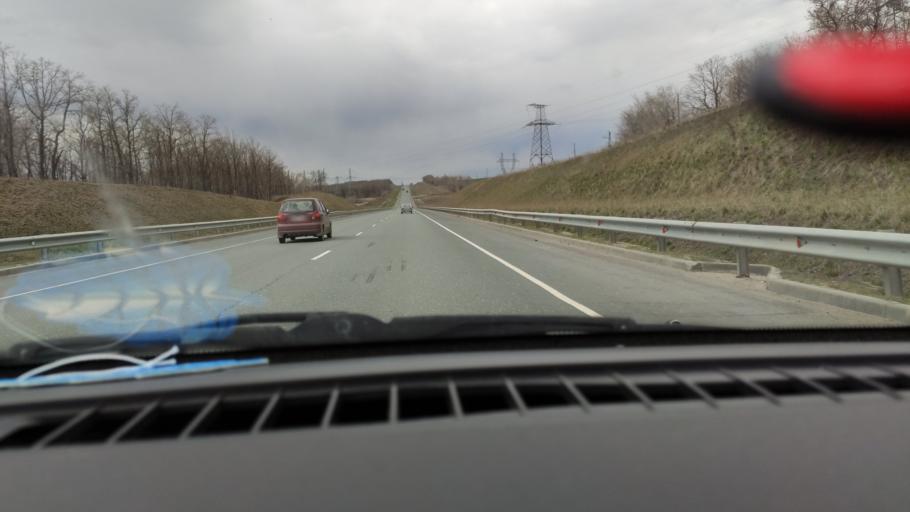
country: RU
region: Saratov
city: Yelshanka
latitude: 51.8232
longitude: 46.3174
